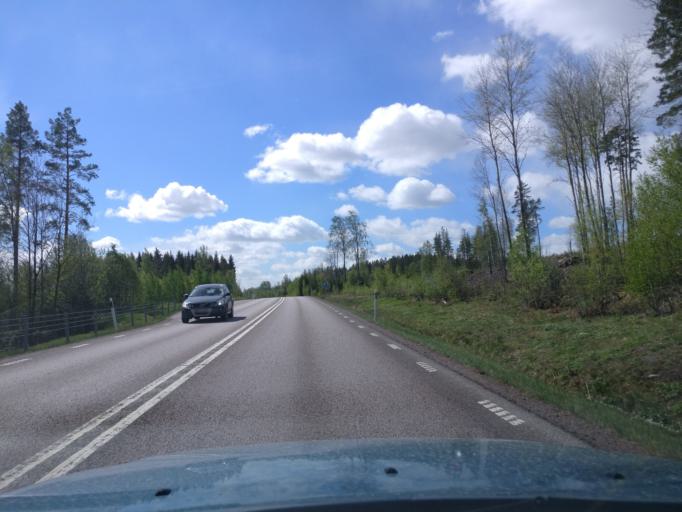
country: SE
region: Vaermland
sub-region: Karlstads Kommun
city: Molkom
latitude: 59.5546
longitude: 13.6624
